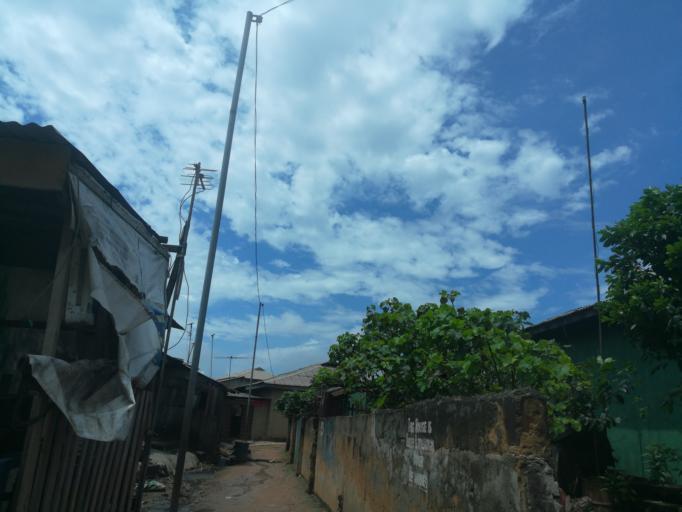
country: NG
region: Lagos
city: Agege
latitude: 6.6153
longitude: 3.3292
